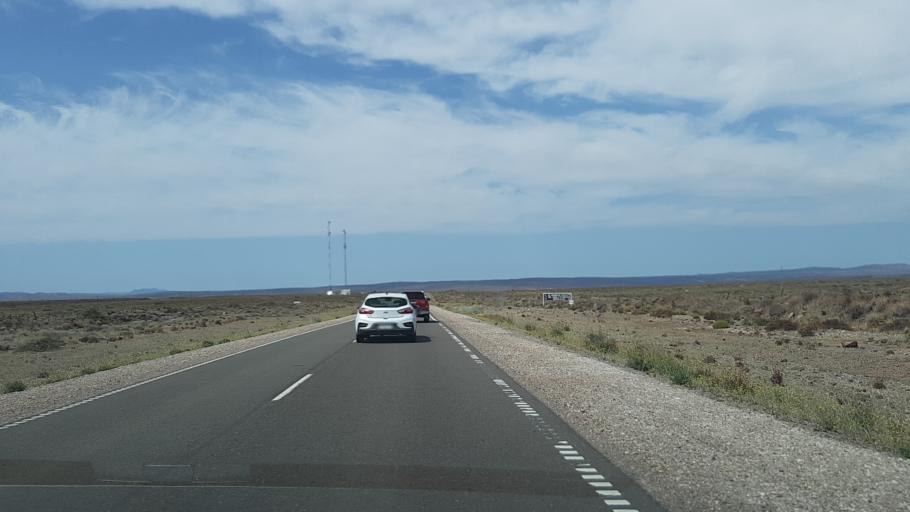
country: AR
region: Neuquen
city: Piedra del Aguila
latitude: -39.9921
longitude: -70.0407
